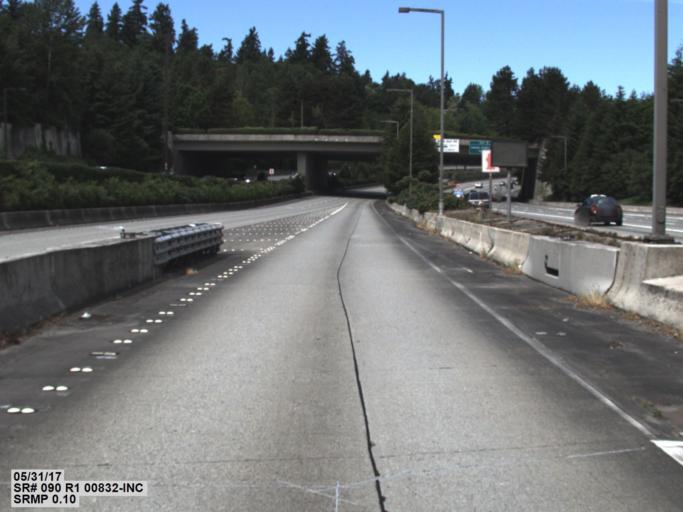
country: US
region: Washington
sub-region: King County
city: Seattle
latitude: 47.5897
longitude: -122.3276
